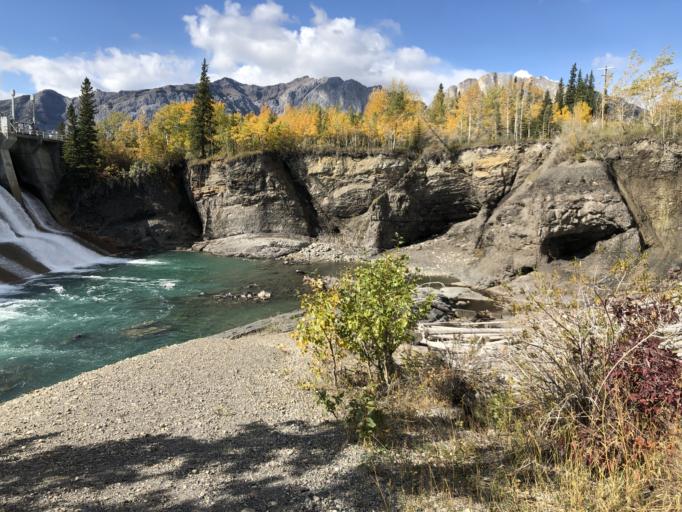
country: CA
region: Alberta
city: Canmore
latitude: 51.0978
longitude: -115.0612
